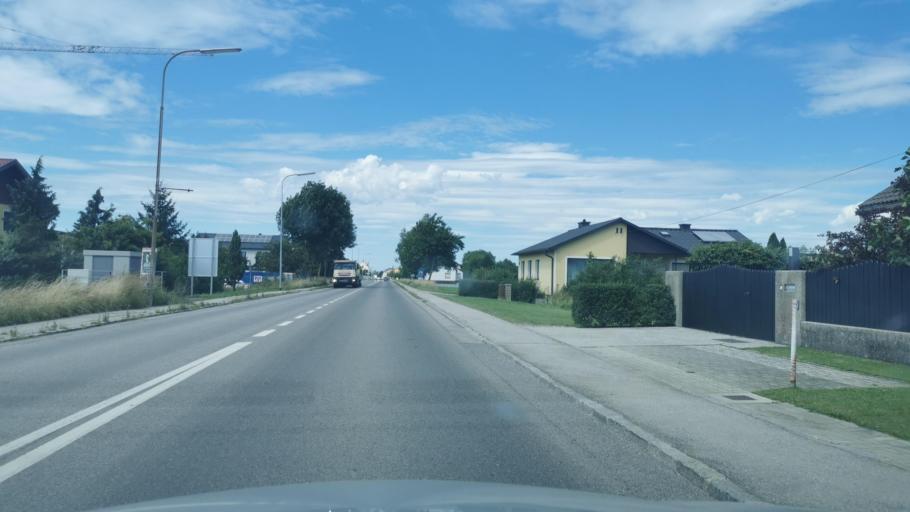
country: AT
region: Lower Austria
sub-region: Politischer Bezirk Sankt Polten
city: Wilhelmsburg
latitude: 48.1330
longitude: 15.6129
